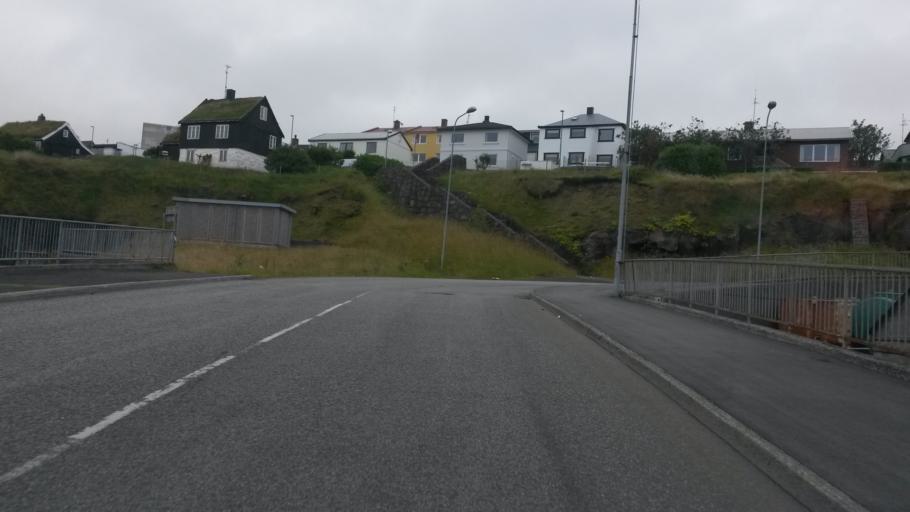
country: FO
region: Streymoy
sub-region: Torshavn
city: Torshavn
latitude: 62.0047
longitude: -6.7755
